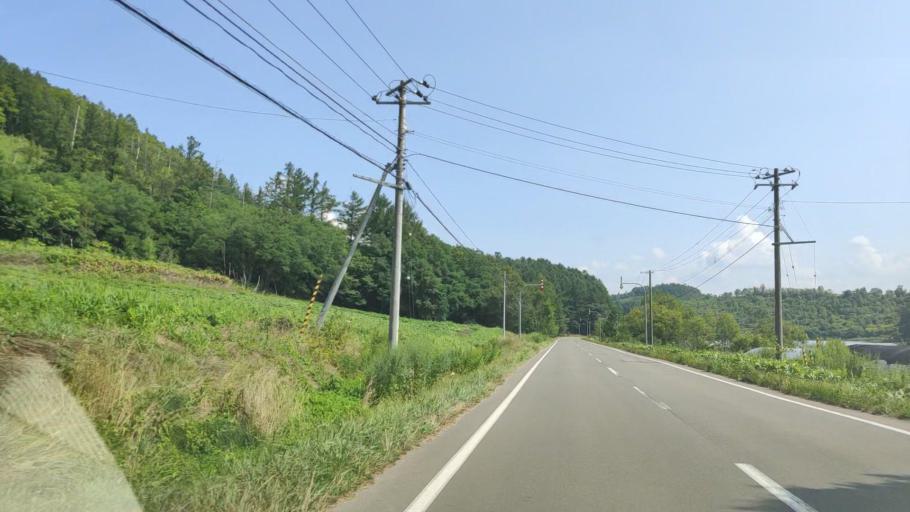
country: JP
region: Hokkaido
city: Shimo-furano
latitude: 43.4285
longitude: 142.4062
